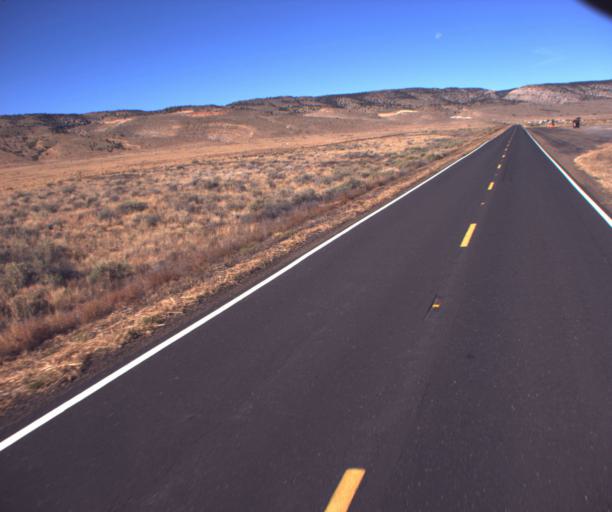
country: US
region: Arizona
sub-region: Coconino County
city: Fredonia
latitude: 36.7285
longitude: -112.0370
